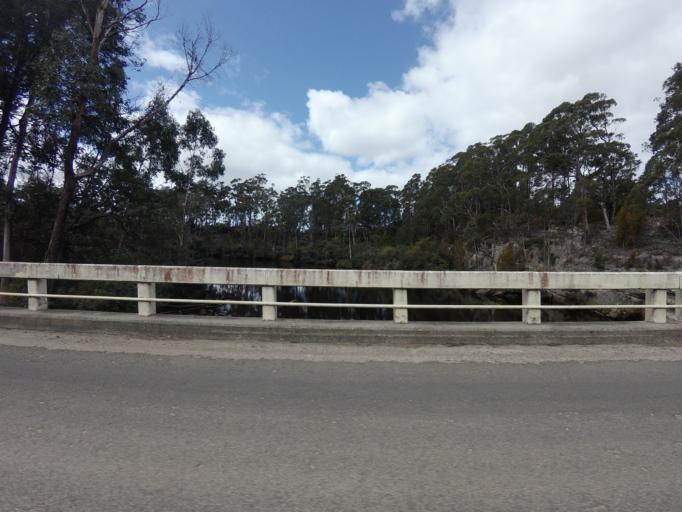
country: AU
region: Tasmania
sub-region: Huon Valley
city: Geeveston
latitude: -43.3306
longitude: 146.9708
